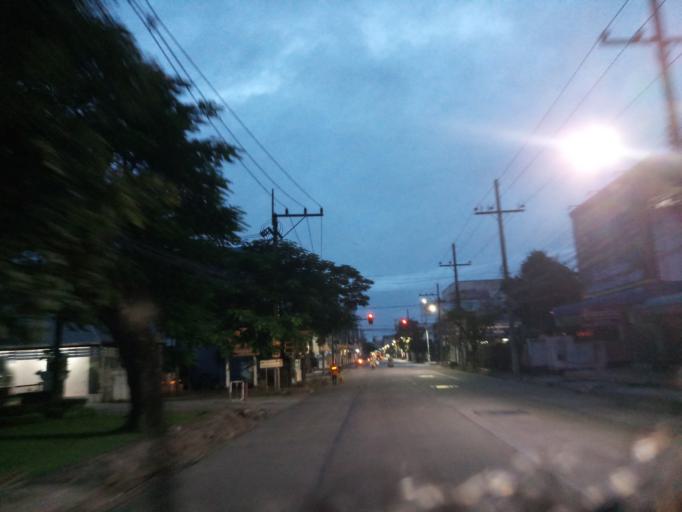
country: TH
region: Chiang Rai
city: Chiang Rai
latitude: 19.9004
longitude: 99.8324
